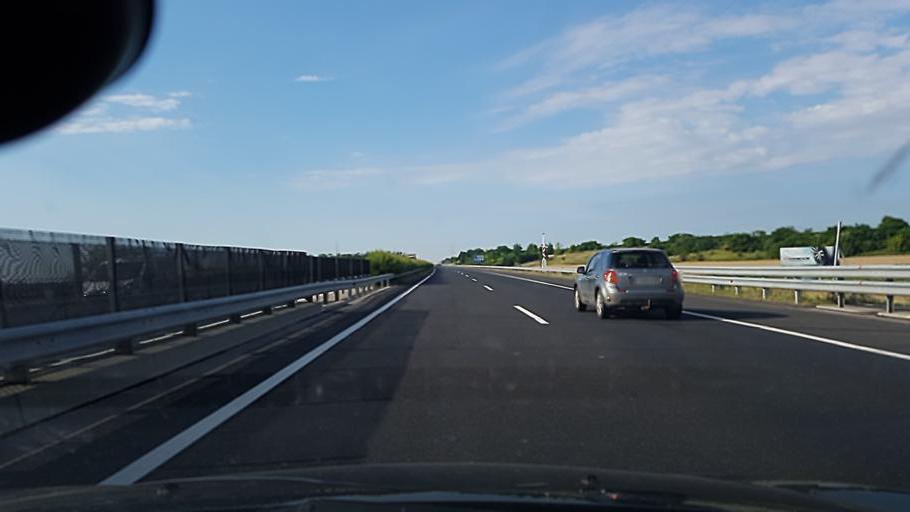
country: HU
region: Fejer
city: Rackeresztur
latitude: 47.2217
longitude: 18.8193
